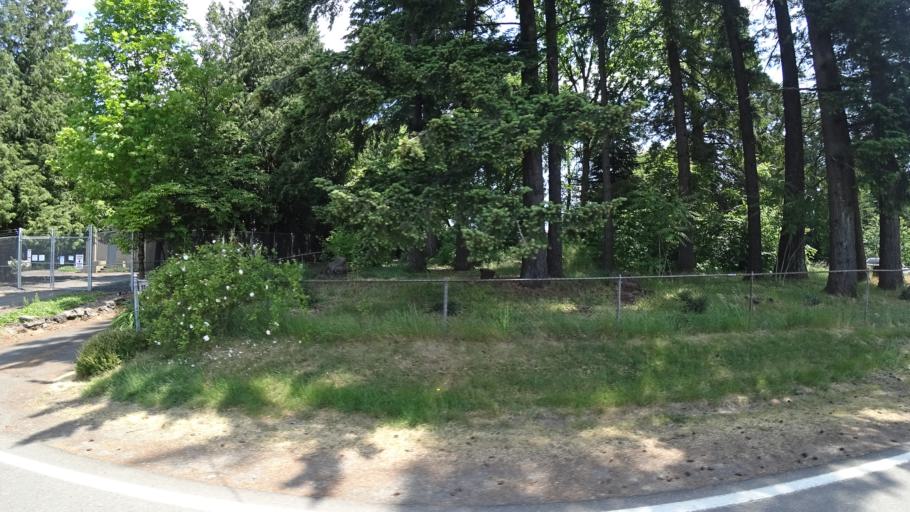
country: US
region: Oregon
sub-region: Clackamas County
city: Happy Valley
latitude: 45.4518
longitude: -122.5482
